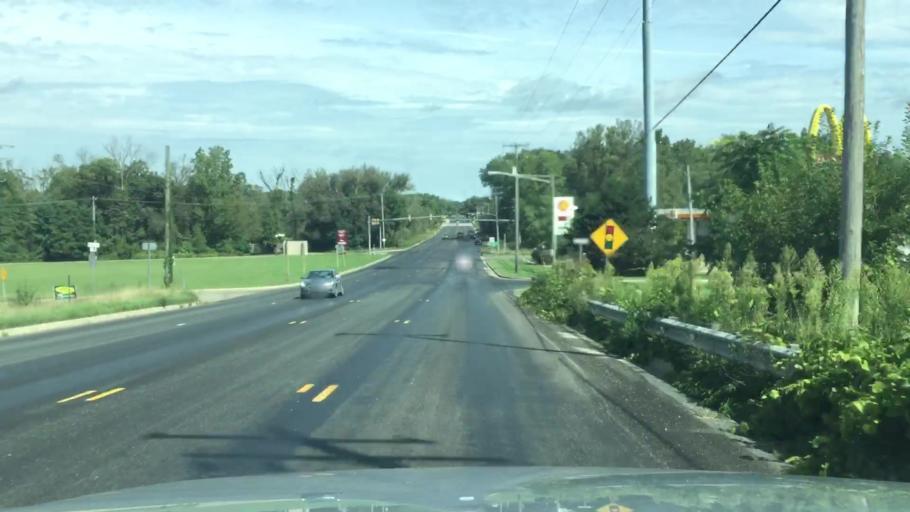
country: US
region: Michigan
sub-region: Kalamazoo County
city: Galesburg
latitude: 42.2748
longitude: -85.4288
